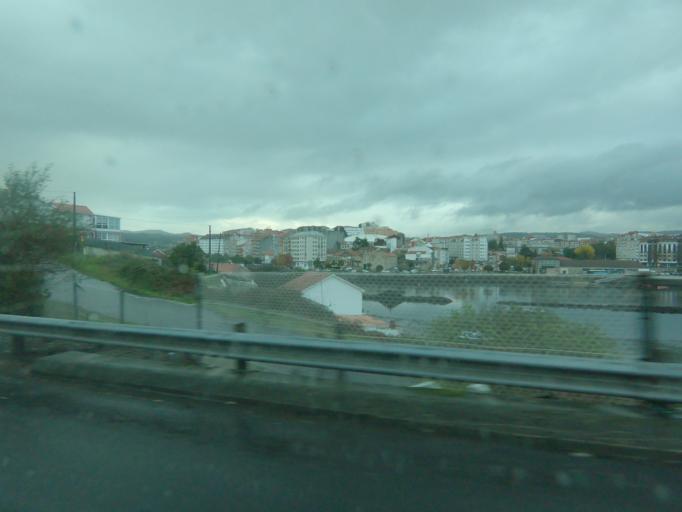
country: ES
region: Galicia
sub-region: Provincia de Pontevedra
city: Poio
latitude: 42.4287
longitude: -8.6561
